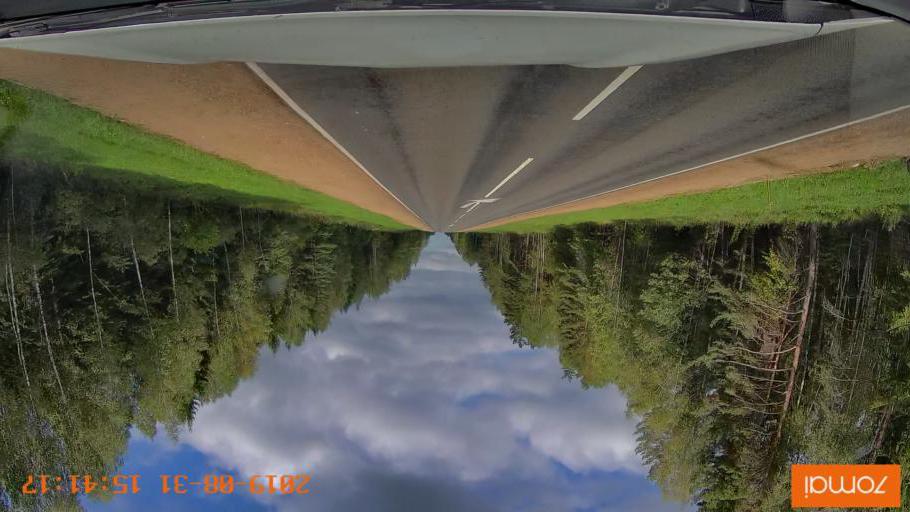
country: RU
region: Kaluga
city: Mosal'sk
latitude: 54.6381
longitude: 34.8566
